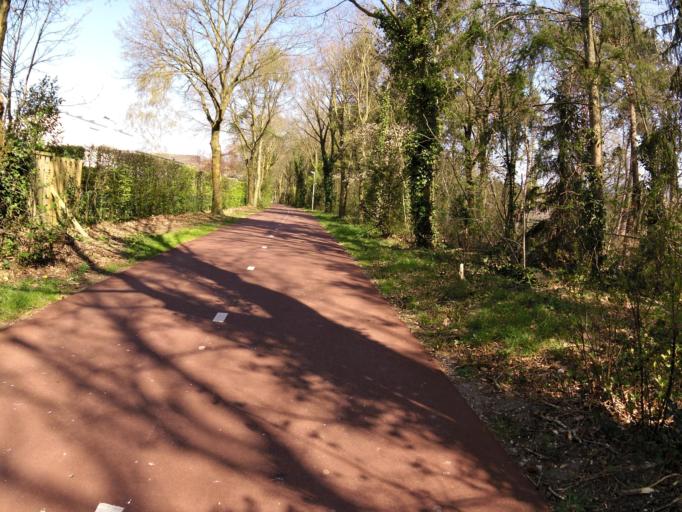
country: NL
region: North Brabant
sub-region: Gemeente Cuijk
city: Cuijk
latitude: 51.7820
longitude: 5.8682
